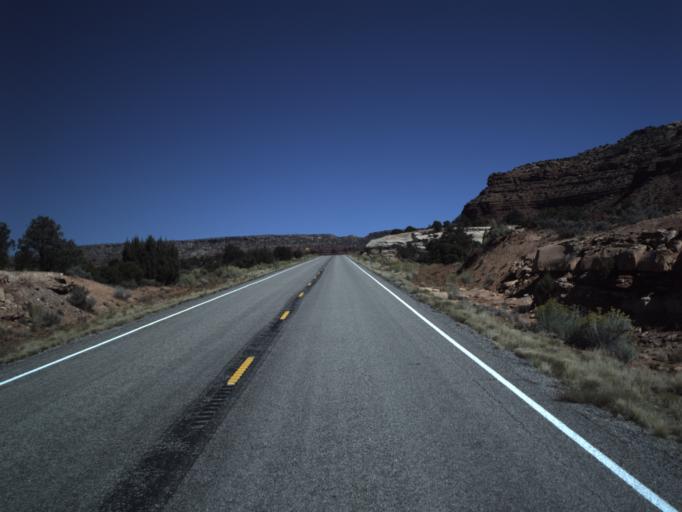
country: US
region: Utah
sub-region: San Juan County
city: Blanding
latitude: 37.6404
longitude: -110.1471
